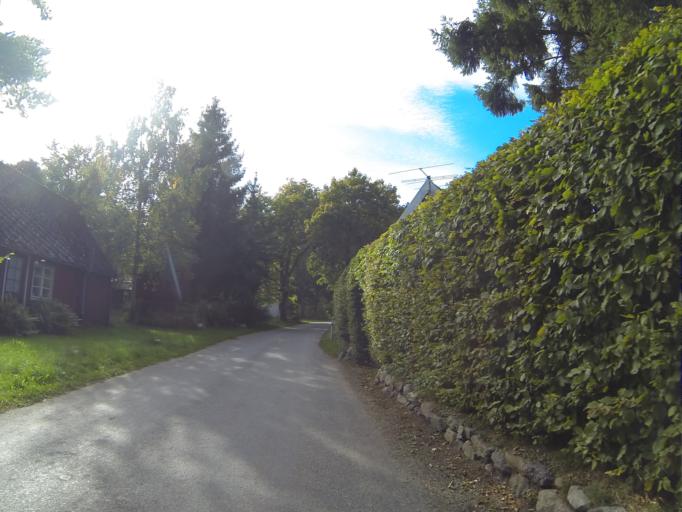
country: SE
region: Skane
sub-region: Eslovs Kommun
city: Eslov
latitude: 55.7343
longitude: 13.3677
